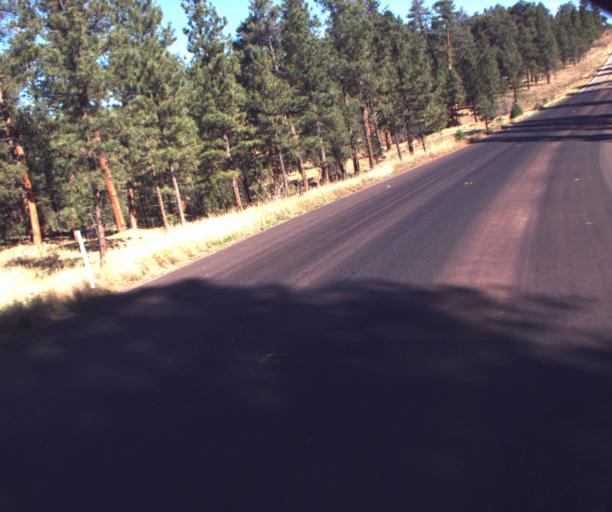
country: US
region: Arizona
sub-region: Coconino County
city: Fredonia
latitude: 36.7557
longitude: -112.2688
